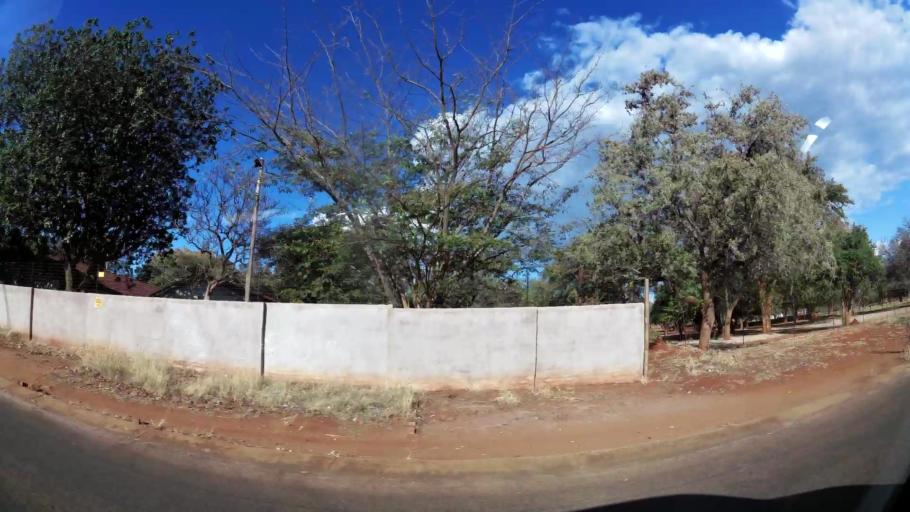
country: ZA
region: Limpopo
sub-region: Waterberg District Municipality
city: Mokopane
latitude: -24.1949
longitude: 29.0043
